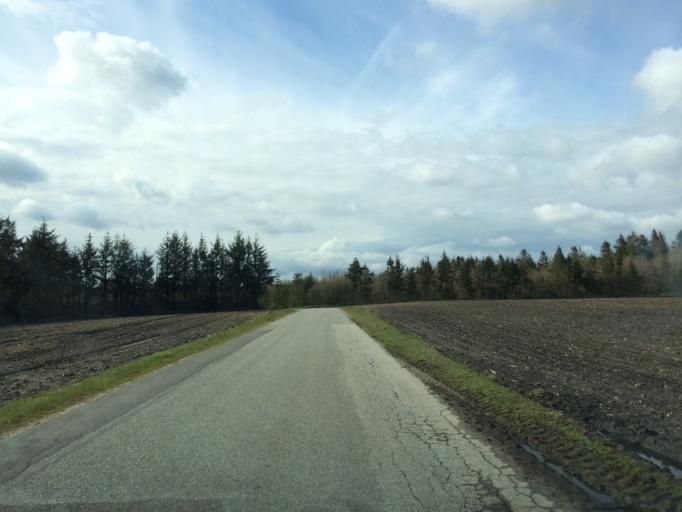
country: DK
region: Central Jutland
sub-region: Ringkobing-Skjern Kommune
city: Videbaek
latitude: 56.2149
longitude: 8.5315
